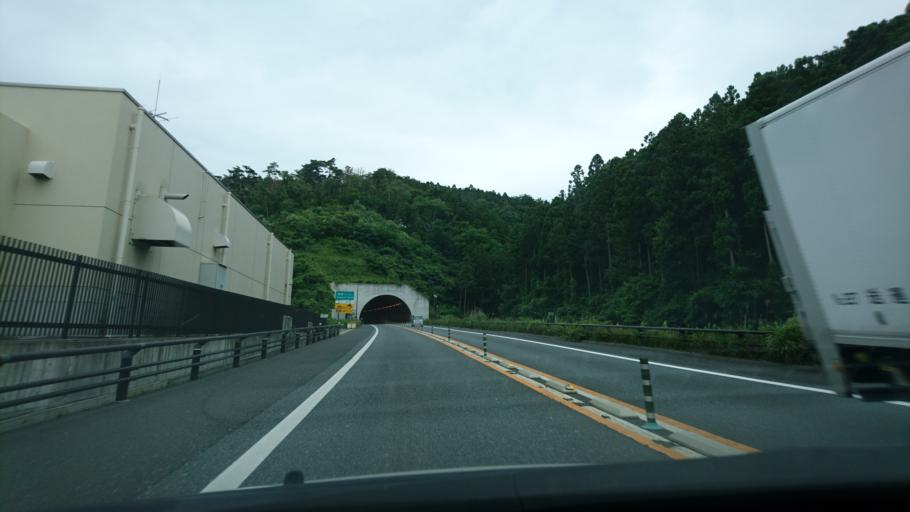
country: JP
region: Miyagi
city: Wakuya
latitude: 38.6261
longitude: 141.2845
